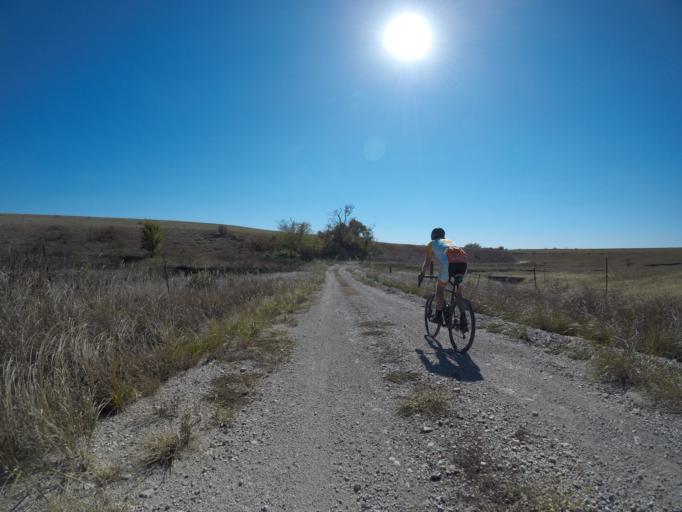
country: US
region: Kansas
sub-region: Wabaunsee County
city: Alma
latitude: 39.0230
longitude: -96.4093
